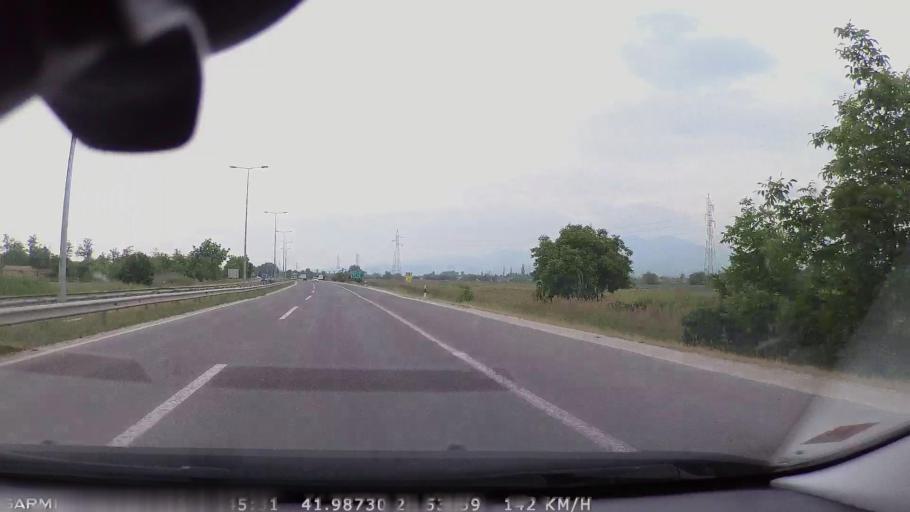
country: MK
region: Ilinden
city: Jurumleri
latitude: 41.9858
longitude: 21.5373
